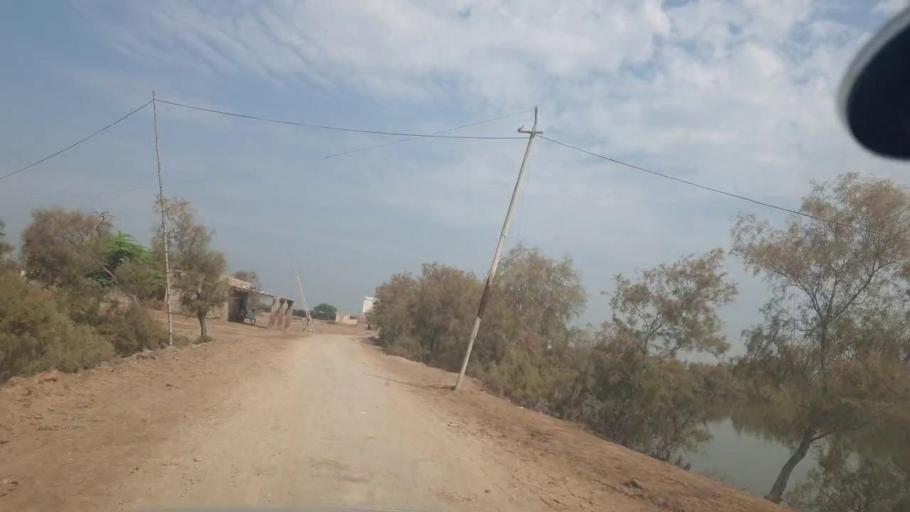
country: PK
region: Balochistan
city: Mehrabpur
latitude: 28.1284
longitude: 68.0880
